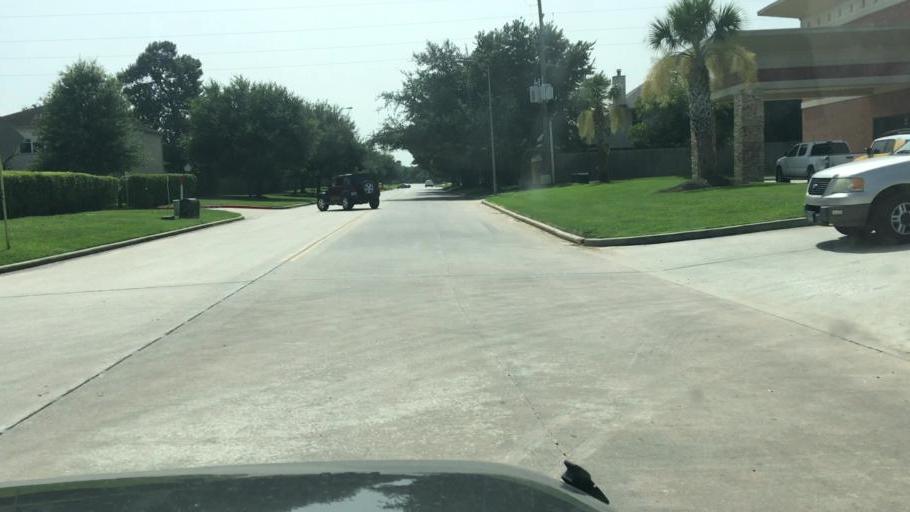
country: US
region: Texas
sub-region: Harris County
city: Atascocita
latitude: 29.9848
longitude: -95.1627
